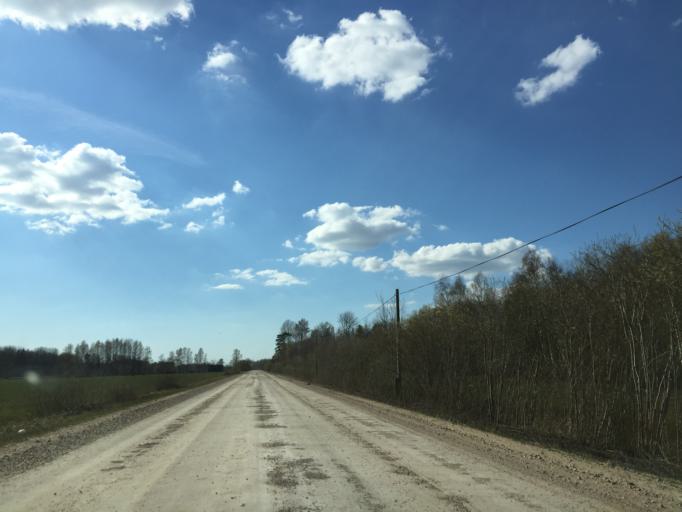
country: LV
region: Krimulda
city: Ragana
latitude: 57.3420
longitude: 24.6114
